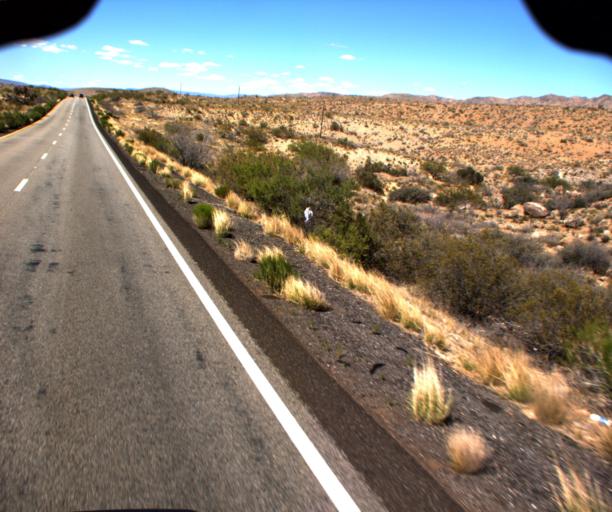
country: US
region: Arizona
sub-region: Mohave County
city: Kingman
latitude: 34.9800
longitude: -113.6680
